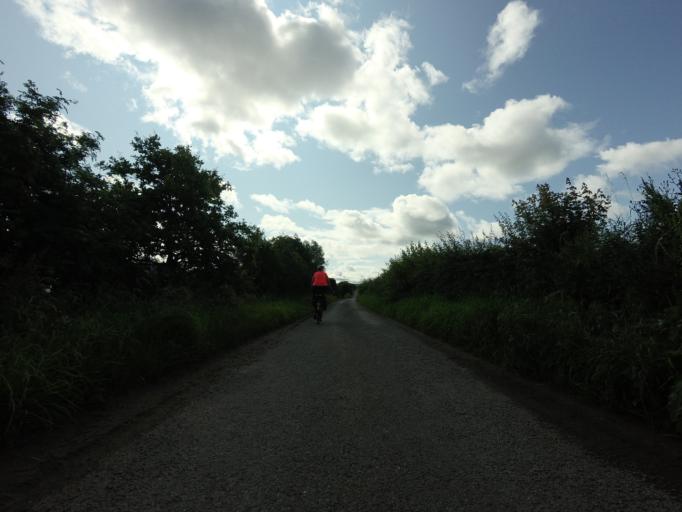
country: GB
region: Scotland
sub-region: Moray
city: Kinloss
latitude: 57.6373
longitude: -3.5196
